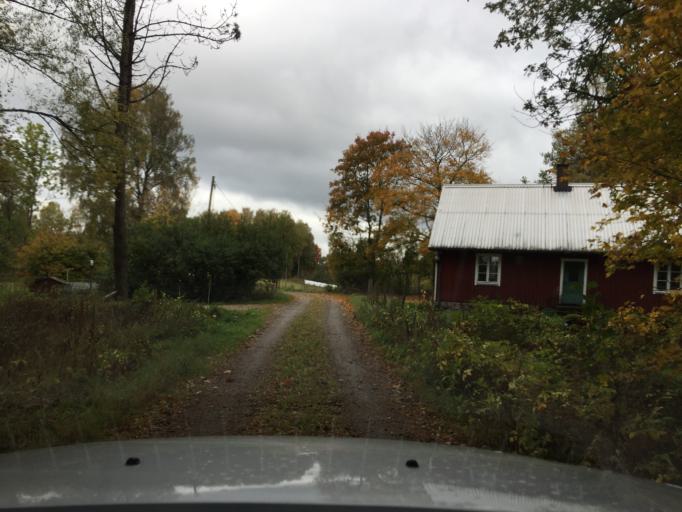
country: SE
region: Skane
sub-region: Hassleholms Kommun
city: Tormestorp
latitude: 56.0663
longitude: 13.7541
